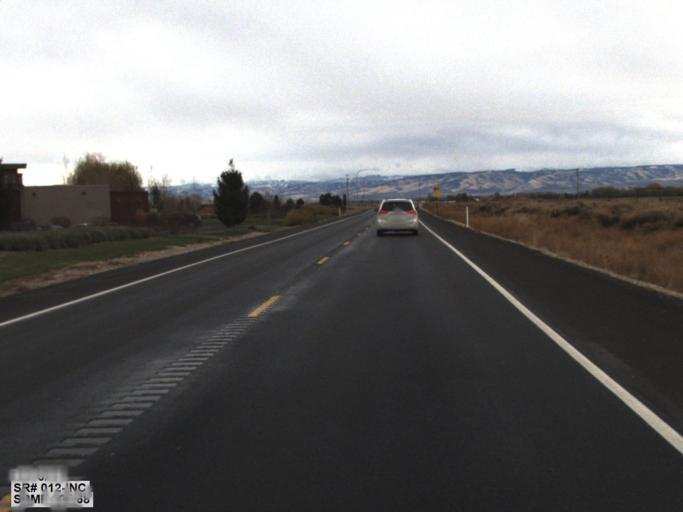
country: US
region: Washington
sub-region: Walla Walla County
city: Garrett
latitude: 46.0534
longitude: -118.5588
